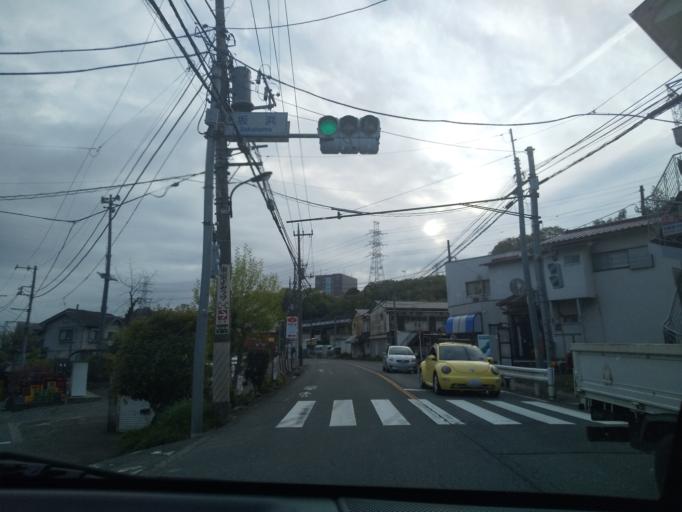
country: JP
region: Tokyo
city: Chofugaoka
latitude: 35.6274
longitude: 139.4878
